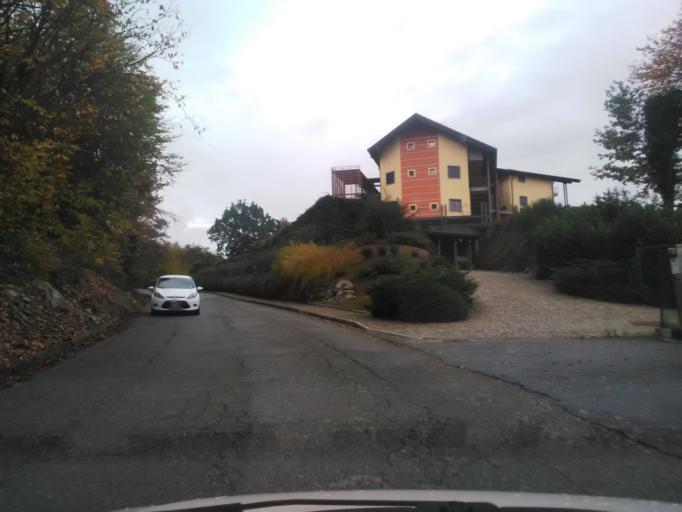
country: IT
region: Piedmont
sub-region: Provincia di Novara
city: Pella
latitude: 45.7991
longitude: 8.3766
